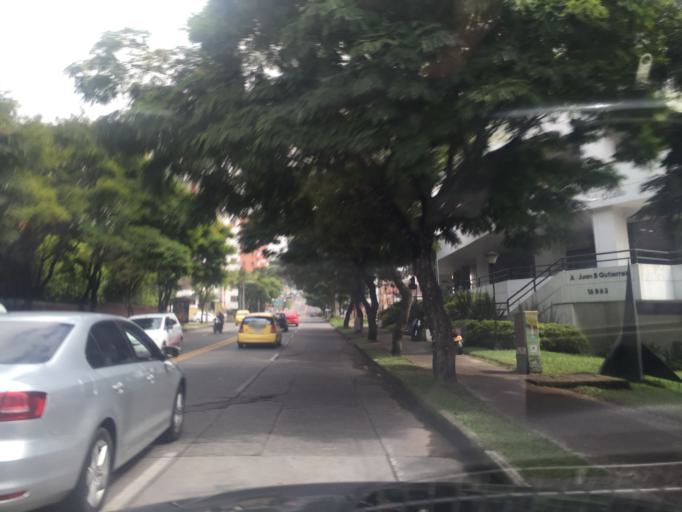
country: CO
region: Risaralda
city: Pereira
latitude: 4.8039
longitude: -75.6841
